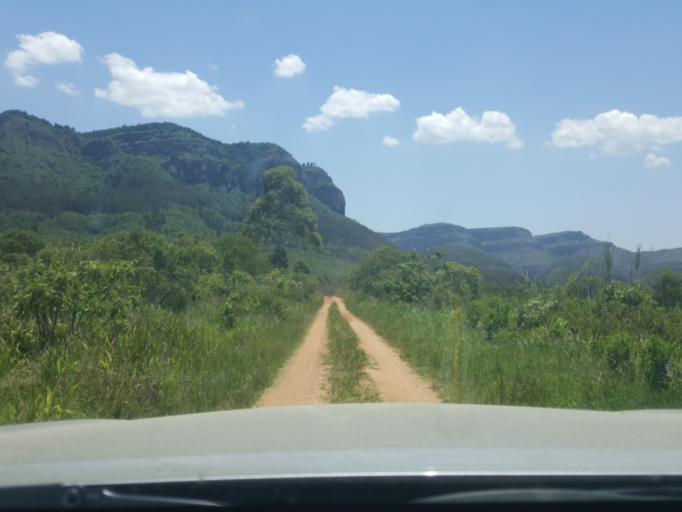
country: ZA
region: Limpopo
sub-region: Mopani District Municipality
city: Hoedspruit
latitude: -24.5945
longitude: 30.8581
